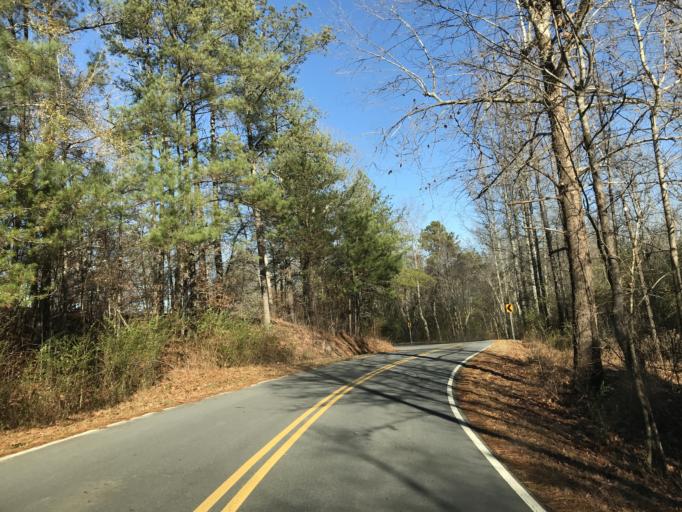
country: US
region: Georgia
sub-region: Paulding County
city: Dallas
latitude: 33.9945
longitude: -84.8935
